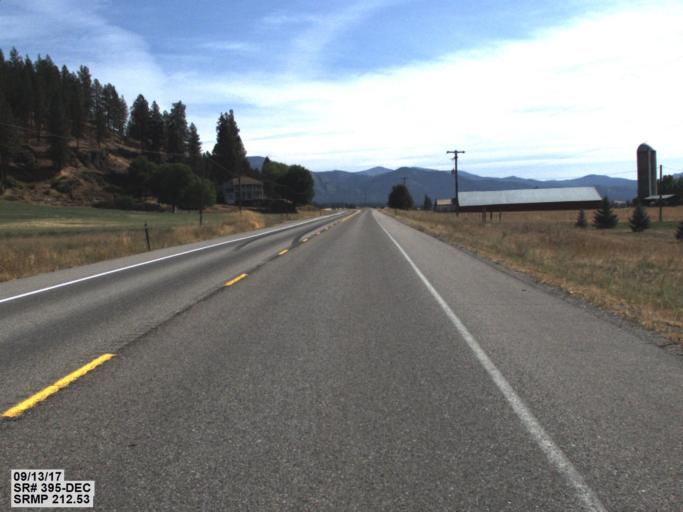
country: US
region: Washington
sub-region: Stevens County
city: Chewelah
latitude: 48.3154
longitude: -117.8091
